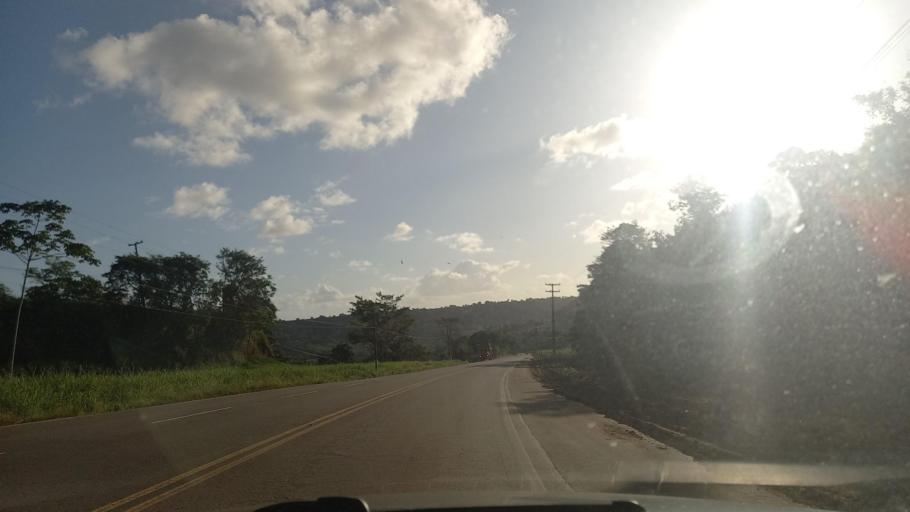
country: BR
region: Alagoas
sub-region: Sao Miguel Dos Campos
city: Sao Miguel dos Campos
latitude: -9.8091
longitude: -36.2122
